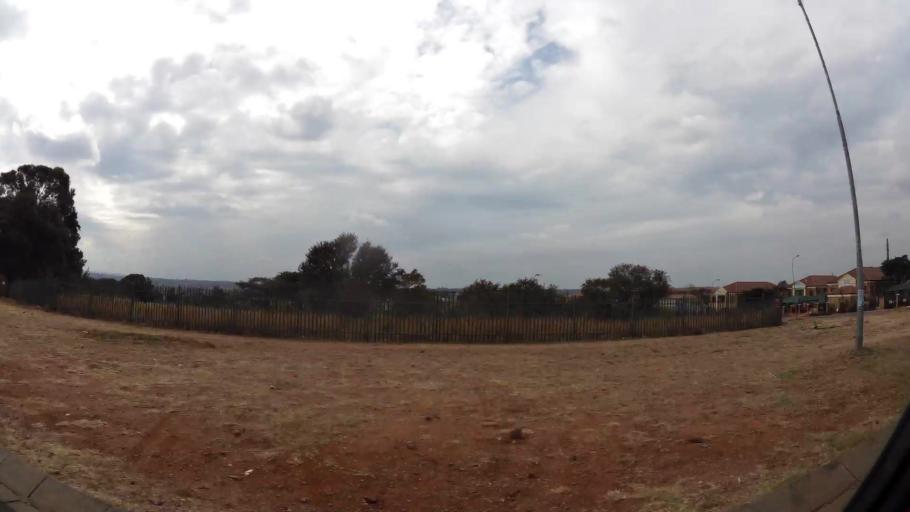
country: ZA
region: Gauteng
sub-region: West Rand District Municipality
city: Muldersdriseloop
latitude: -26.0892
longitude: 27.8691
